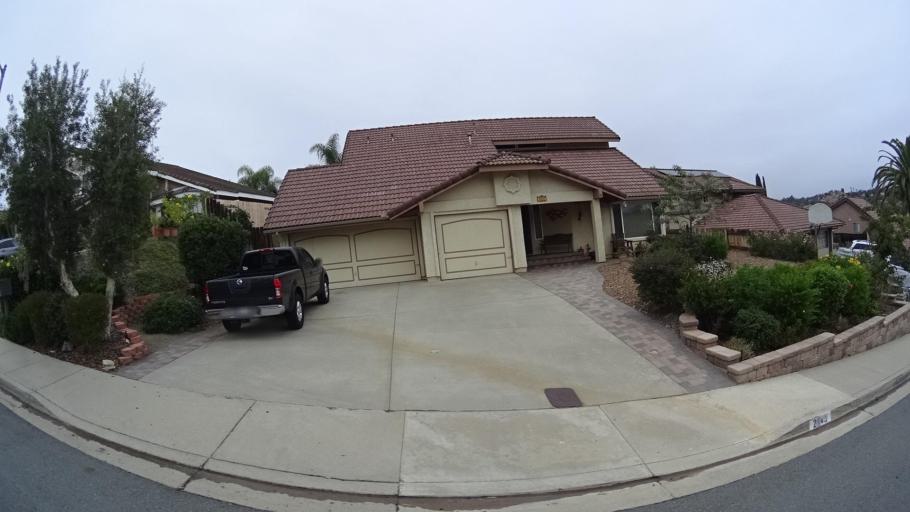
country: US
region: California
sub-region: San Diego County
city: Rancho San Diego
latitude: 32.7567
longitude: -116.9086
